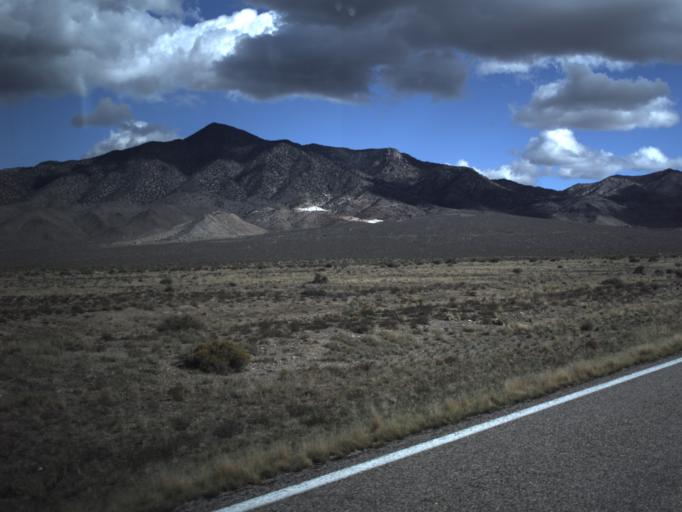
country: US
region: Utah
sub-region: Beaver County
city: Milford
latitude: 38.4518
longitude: -113.3496
